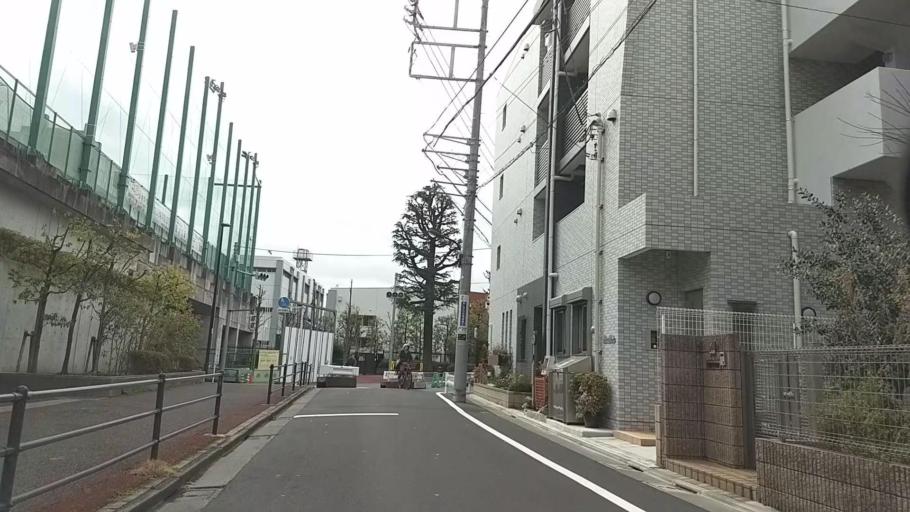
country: JP
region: Tokyo
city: Tokyo
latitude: 35.6104
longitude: 139.7204
